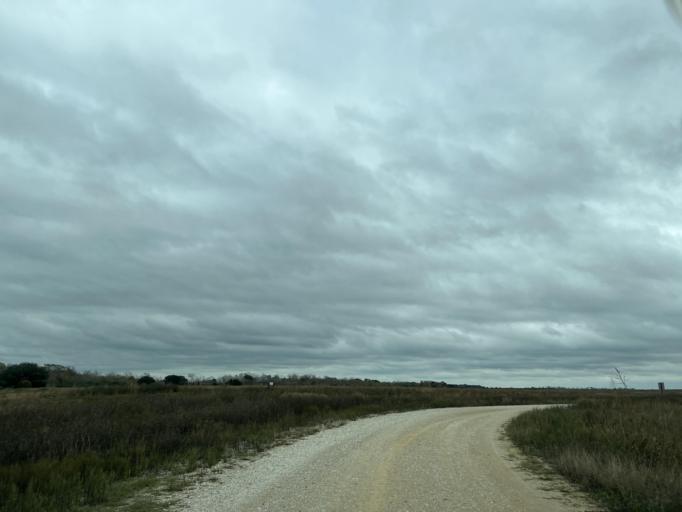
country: US
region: Texas
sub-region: Colorado County
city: Eagle Lake
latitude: 29.6713
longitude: -96.2672
